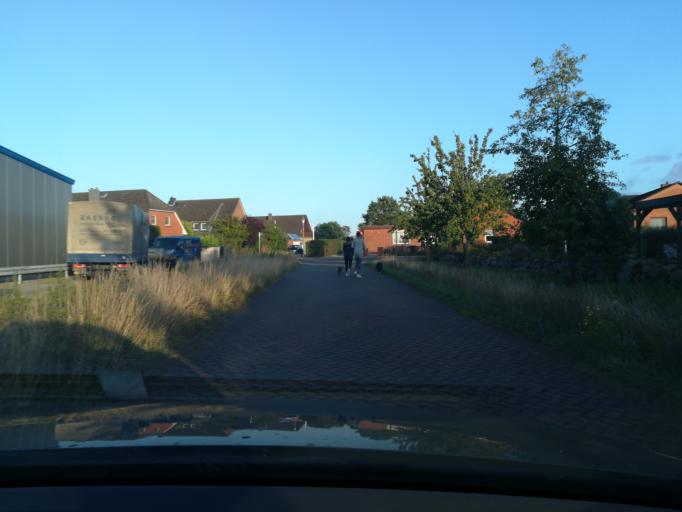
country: DE
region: Lower Saxony
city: Artlenburg
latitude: 53.3700
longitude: 10.4800
